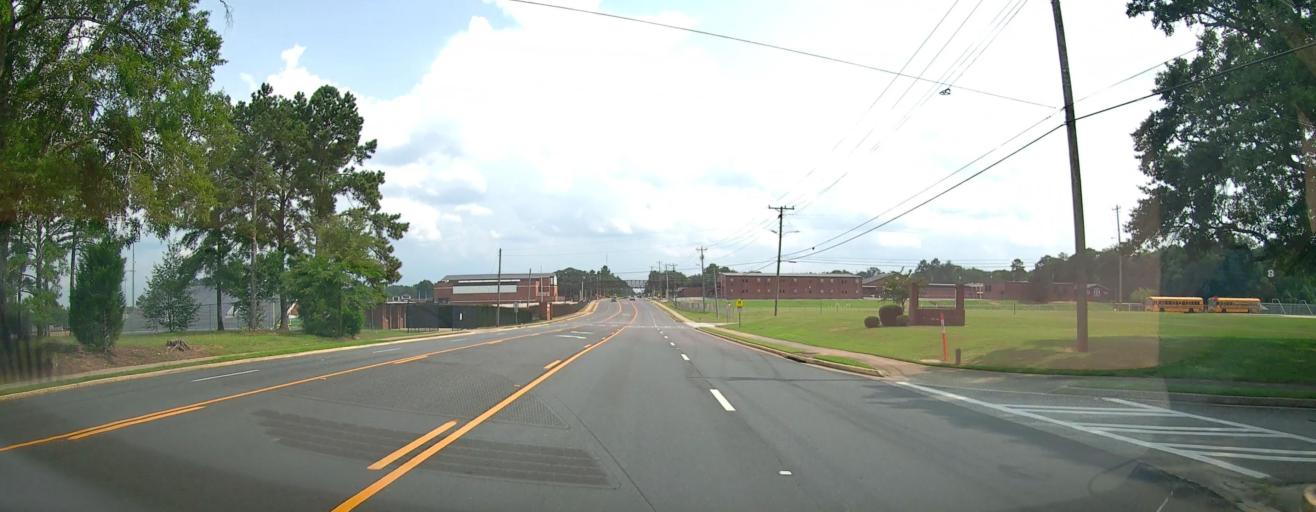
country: US
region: Georgia
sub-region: Houston County
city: Warner Robins
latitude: 32.6134
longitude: -83.6132
